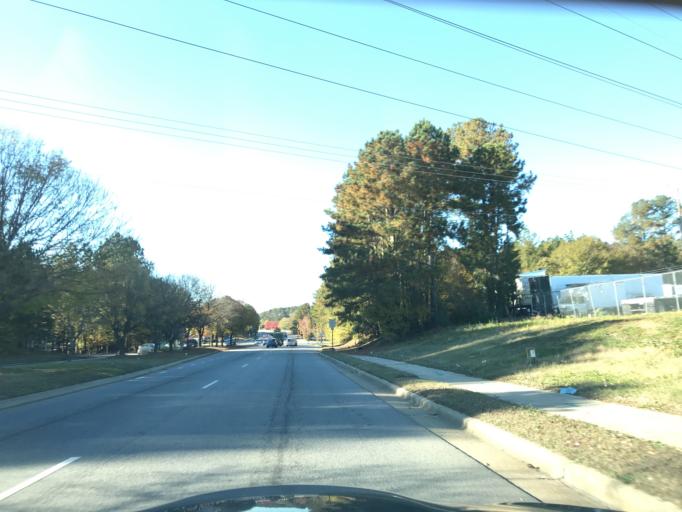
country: US
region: North Carolina
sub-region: Wake County
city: Garner
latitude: 35.7642
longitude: -78.5574
